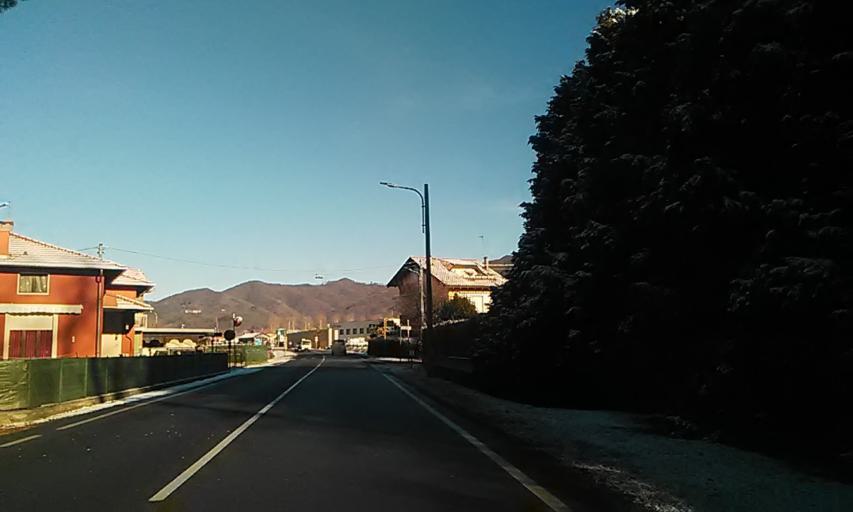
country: IT
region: Piedmont
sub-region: Provincia di Novara
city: Grignasco
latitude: 45.6659
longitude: 8.3540
